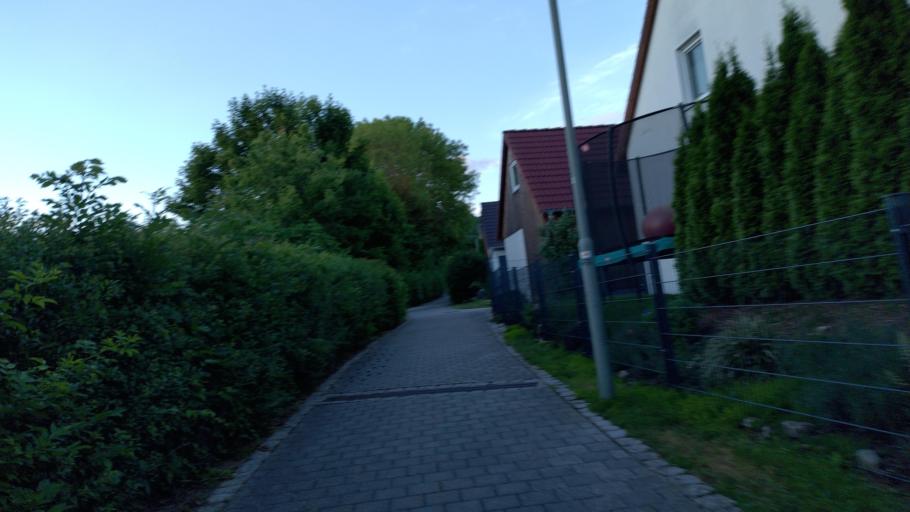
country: DE
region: Bavaria
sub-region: Upper Franconia
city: Bindlach
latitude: 49.9841
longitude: 11.6186
